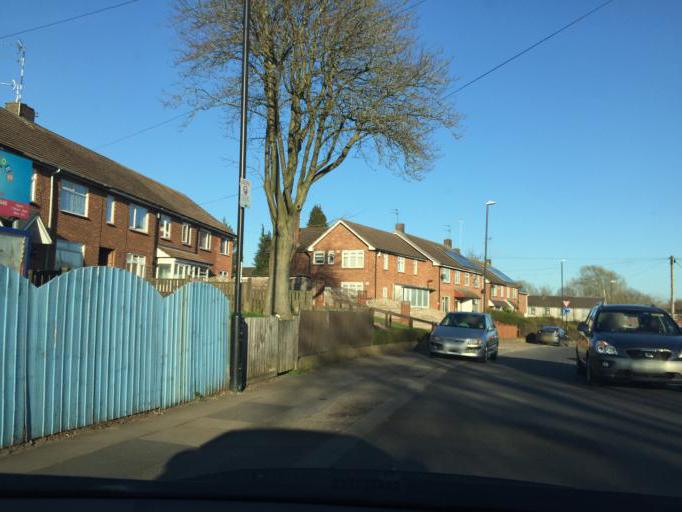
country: GB
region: England
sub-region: Coventry
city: Coventry
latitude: 52.3974
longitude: -1.4725
